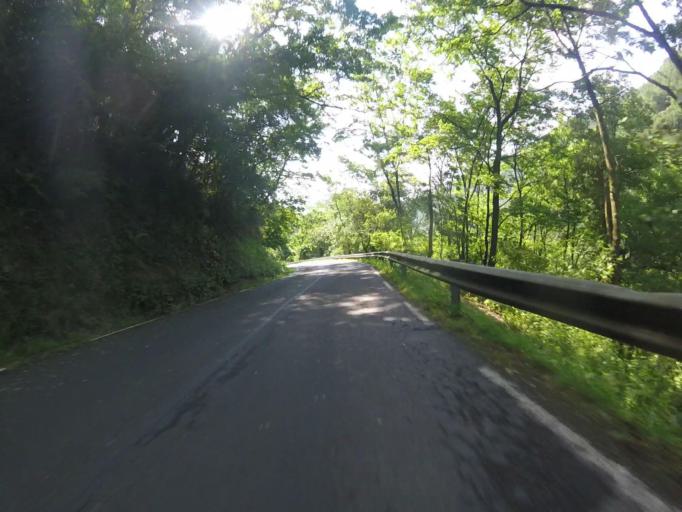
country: ES
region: Basque Country
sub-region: Provincia de Guipuzcoa
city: Hernialde
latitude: 43.1649
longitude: -2.0906
